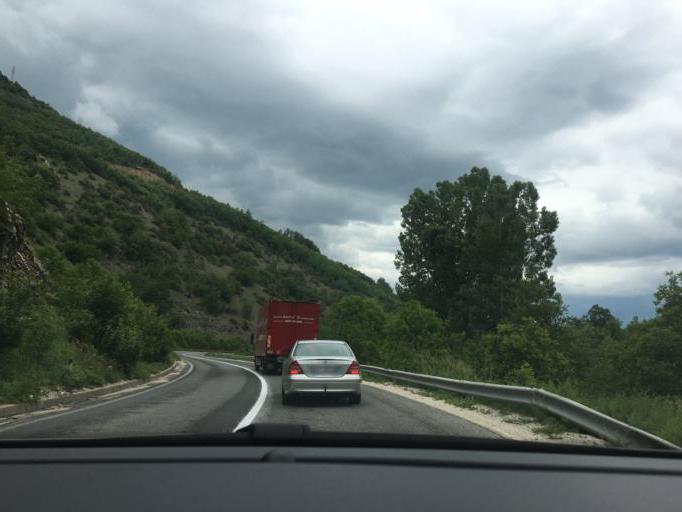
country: MK
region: Drugovo
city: Drugovo
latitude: 41.4769
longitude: 20.8731
